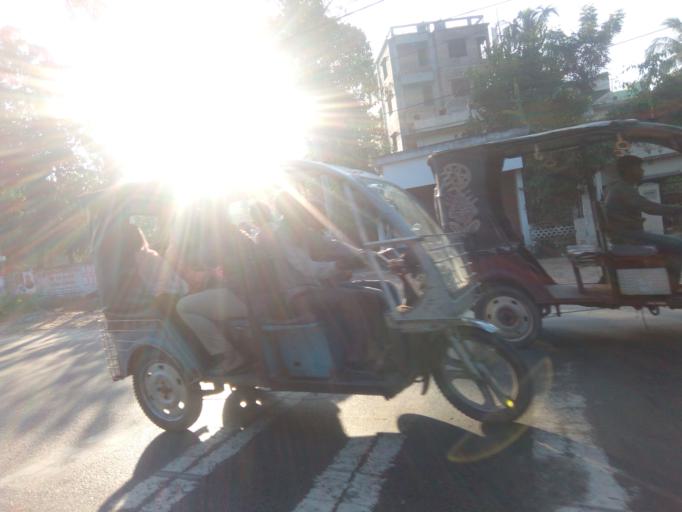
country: BD
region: Rajshahi
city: Rajshahi
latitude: 24.3622
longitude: 88.6288
